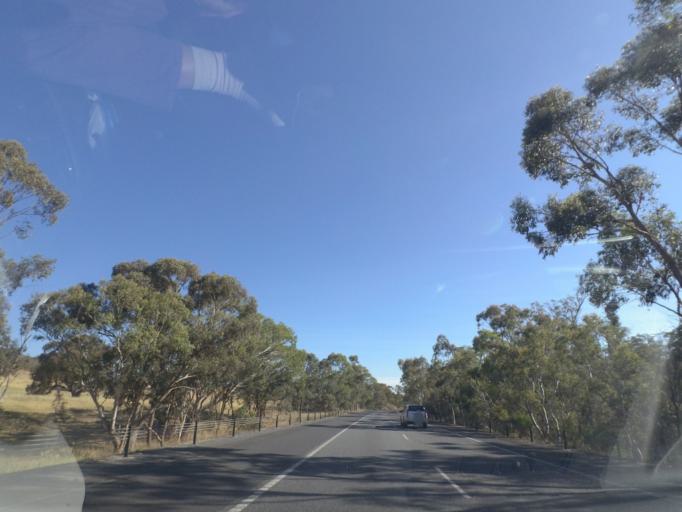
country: AU
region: Victoria
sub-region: Murrindindi
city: Kinglake West
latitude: -37.1664
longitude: 145.0779
